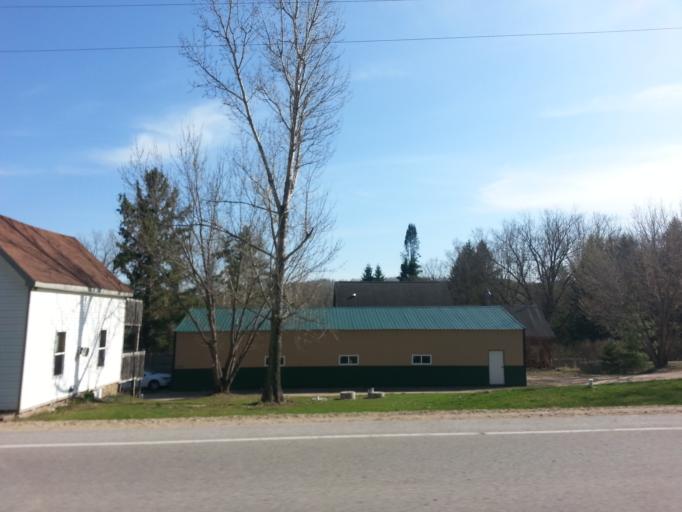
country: US
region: Wisconsin
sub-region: Pierce County
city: Ellsworth
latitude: 44.7730
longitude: -92.5015
